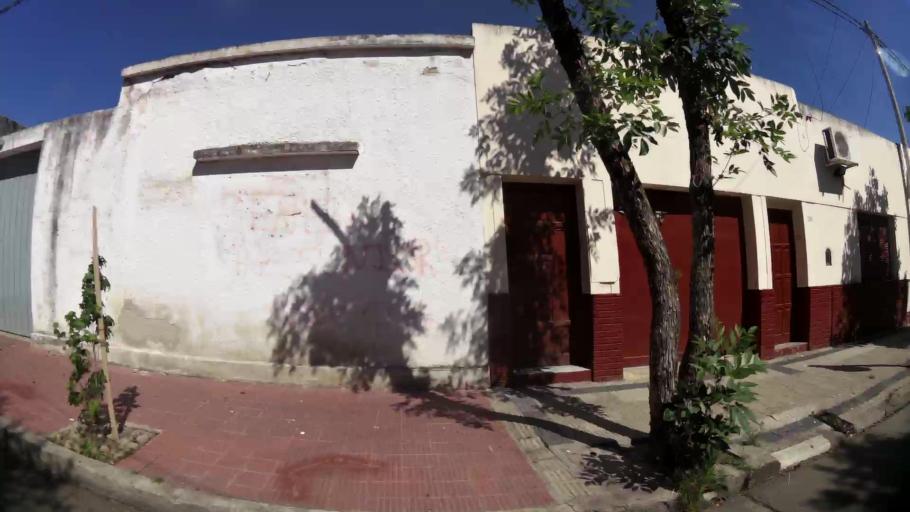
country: AR
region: Cordoba
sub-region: Departamento de Capital
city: Cordoba
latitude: -31.4171
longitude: -64.1618
